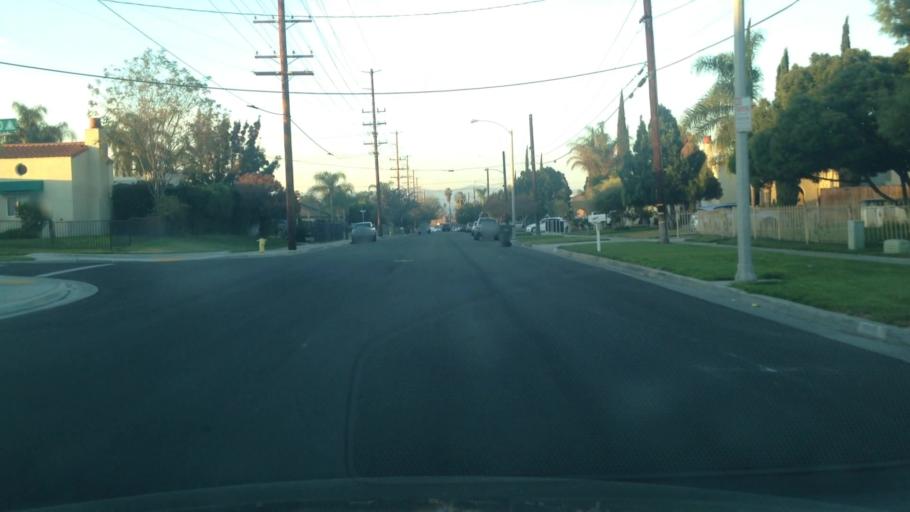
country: US
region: California
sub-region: Riverside County
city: Riverside
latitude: 33.9313
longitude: -117.4052
